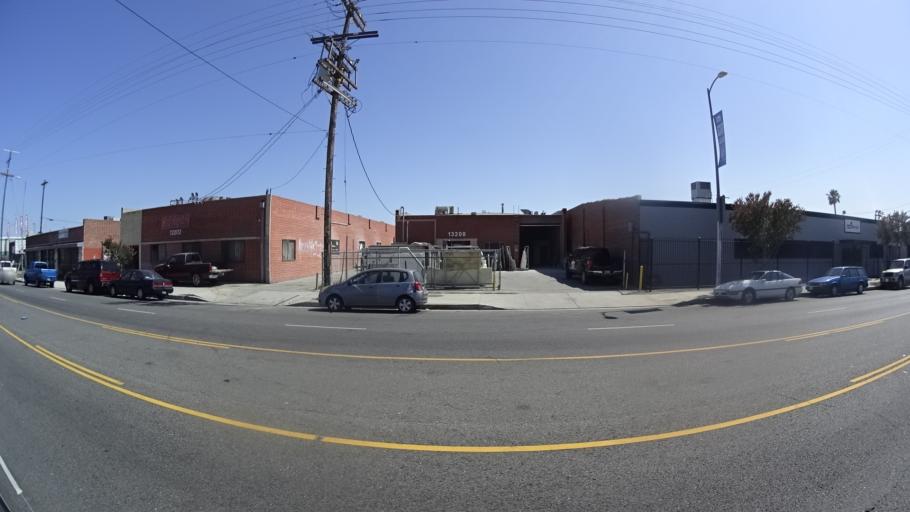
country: US
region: California
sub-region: Los Angeles County
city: Van Nuys
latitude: 34.2079
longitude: -118.4205
